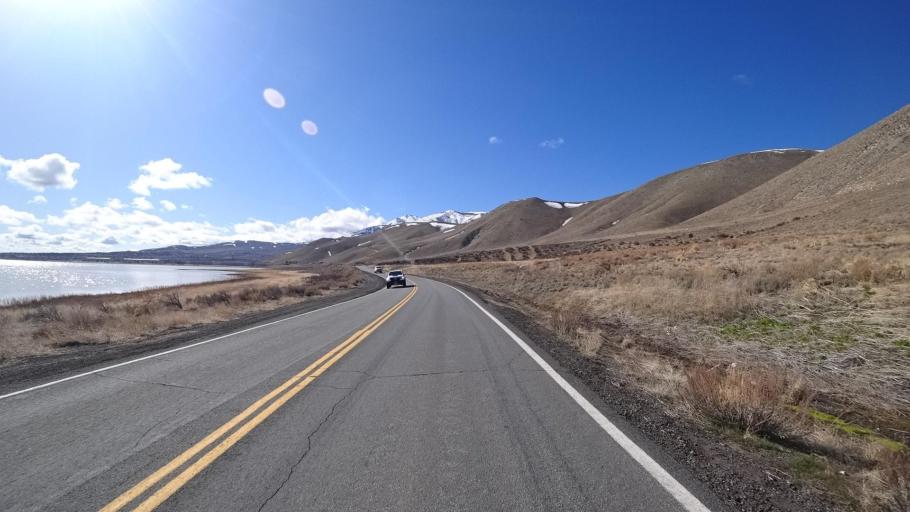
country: US
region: Nevada
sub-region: Washoe County
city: Cold Springs
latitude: 39.6497
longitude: -119.9275
